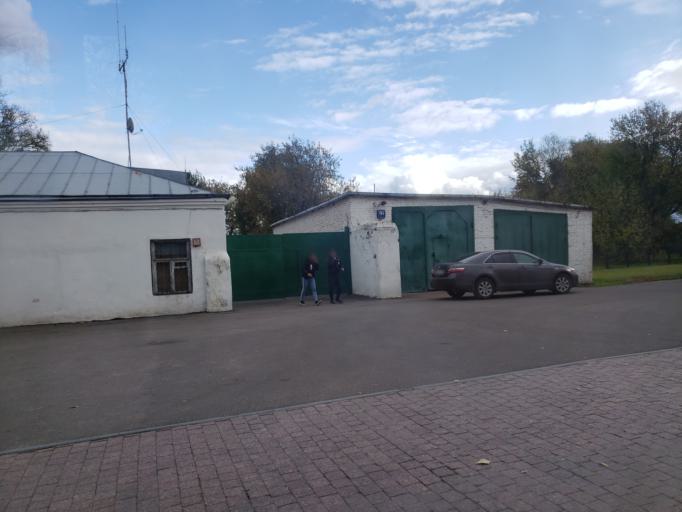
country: RU
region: Moscow
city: Kolomenskoye
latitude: 55.6737
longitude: 37.6701
